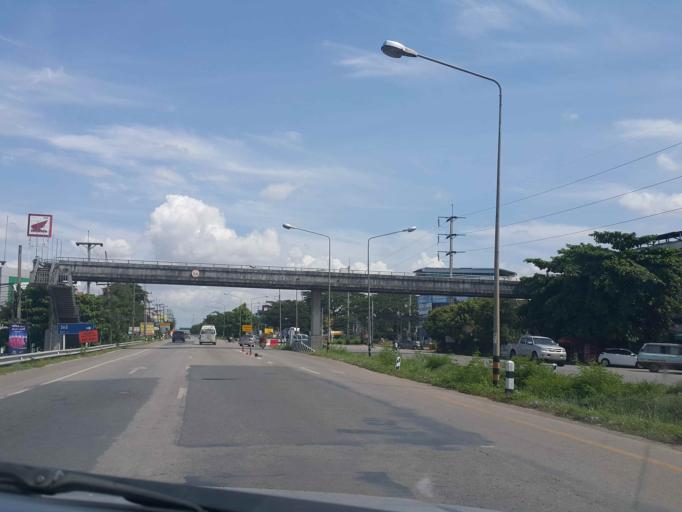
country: TH
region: Phayao
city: Phayao
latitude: 19.1630
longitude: 99.9129
